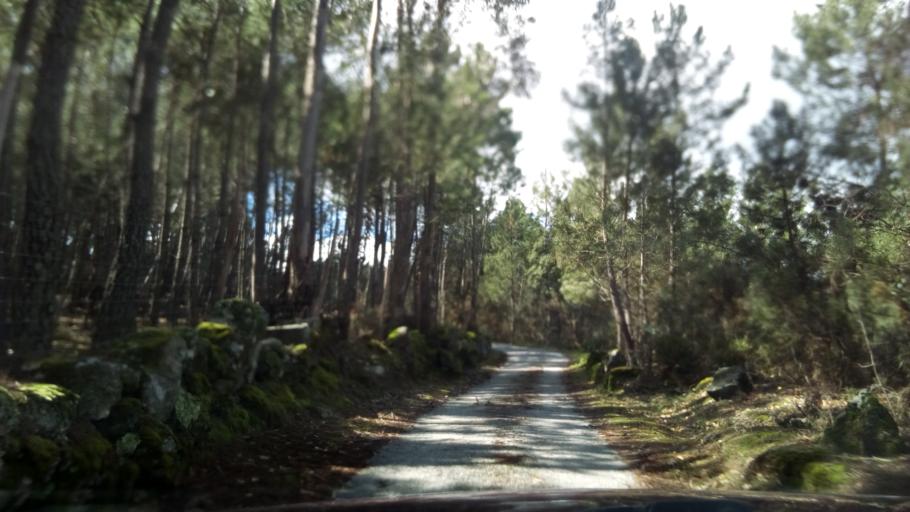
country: PT
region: Guarda
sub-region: Fornos de Algodres
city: Fornos de Algodres
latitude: 40.6270
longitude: -7.5223
